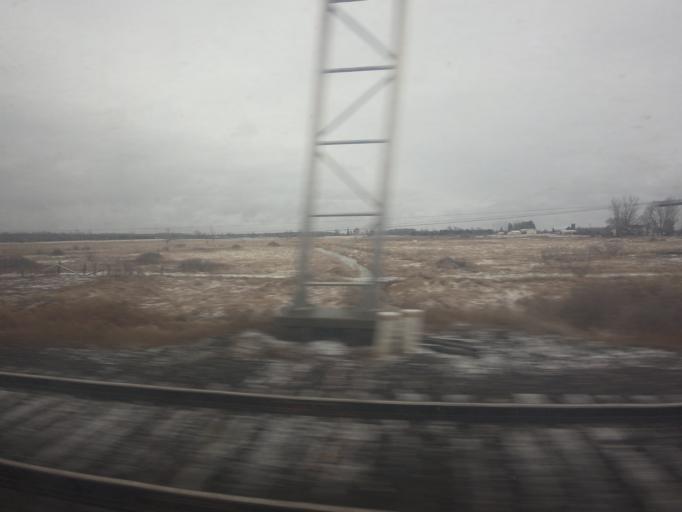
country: CA
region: Ontario
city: Gananoque
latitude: 44.3749
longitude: -76.0975
